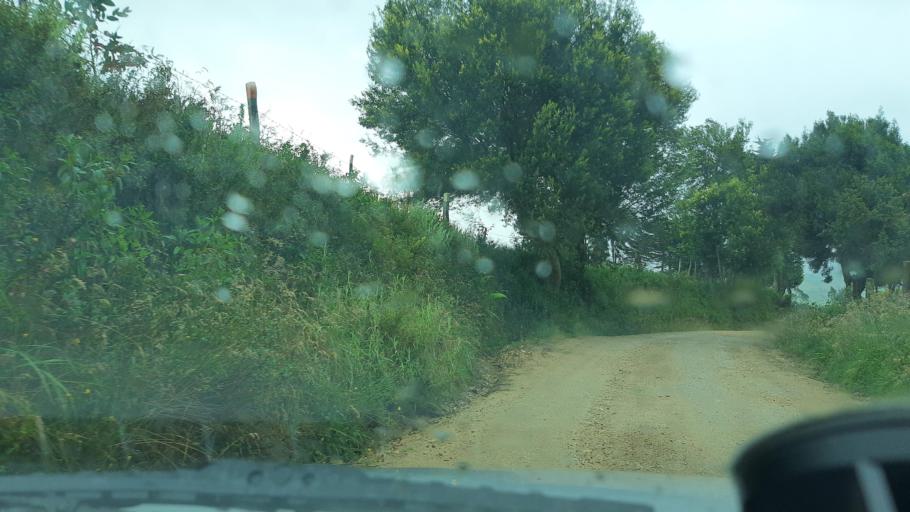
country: CO
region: Cundinamarca
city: Villapinzon
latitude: 5.2201
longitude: -73.5736
